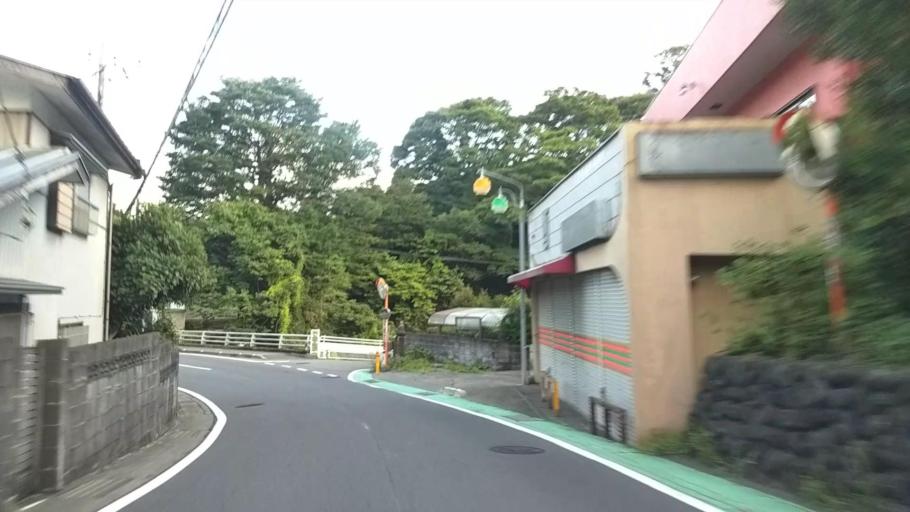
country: JP
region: Kanagawa
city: Atsugi
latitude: 35.4846
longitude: 139.2734
